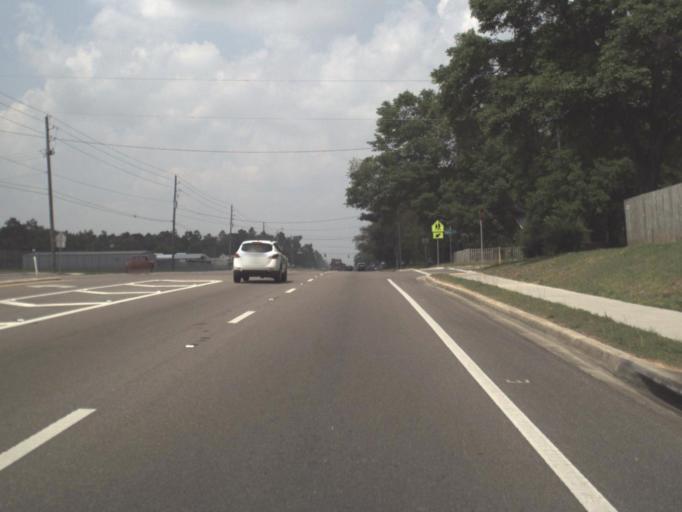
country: US
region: Florida
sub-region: Santa Rosa County
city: Milton
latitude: 30.6420
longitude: -87.0553
